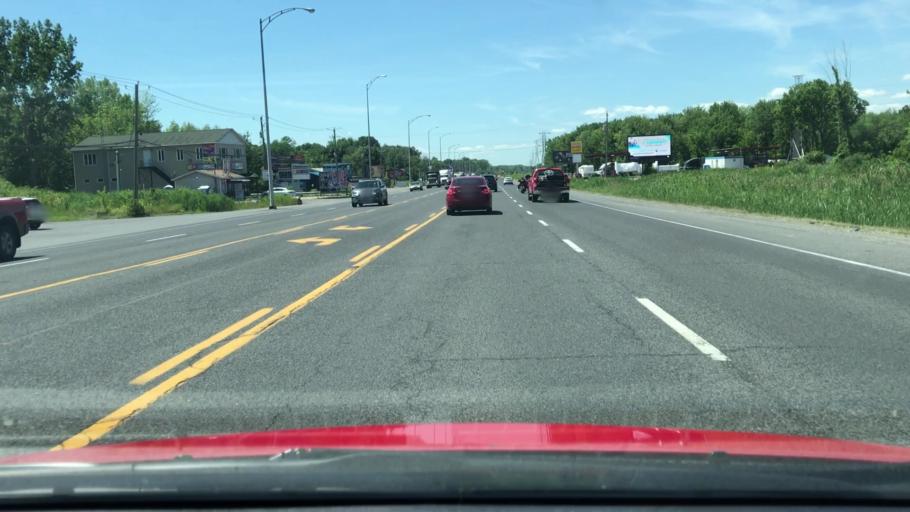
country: CA
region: Quebec
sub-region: Monteregie
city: Saint-Constant
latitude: 45.3975
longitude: -73.6192
